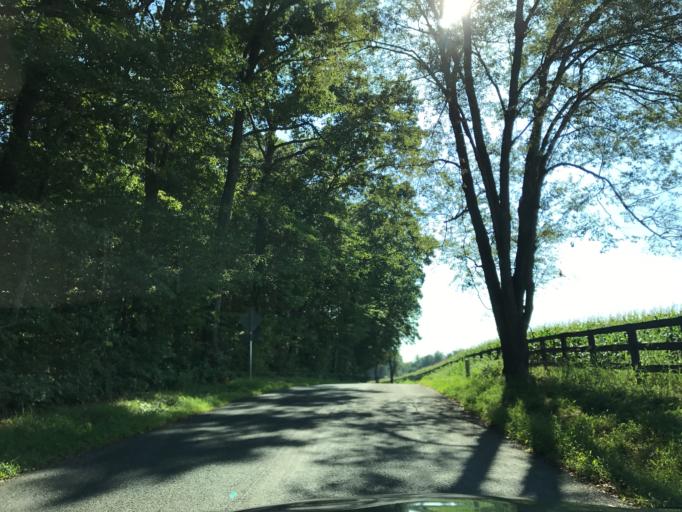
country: US
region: Pennsylvania
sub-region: York County
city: Stewartstown
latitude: 39.6671
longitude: -76.5613
